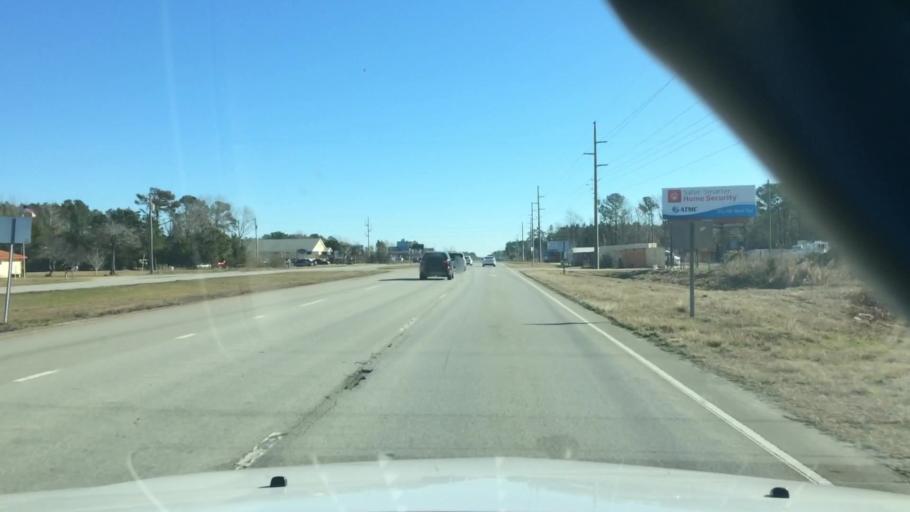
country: US
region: North Carolina
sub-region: Brunswick County
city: Sunset Beach
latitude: 33.9496
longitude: -78.4806
